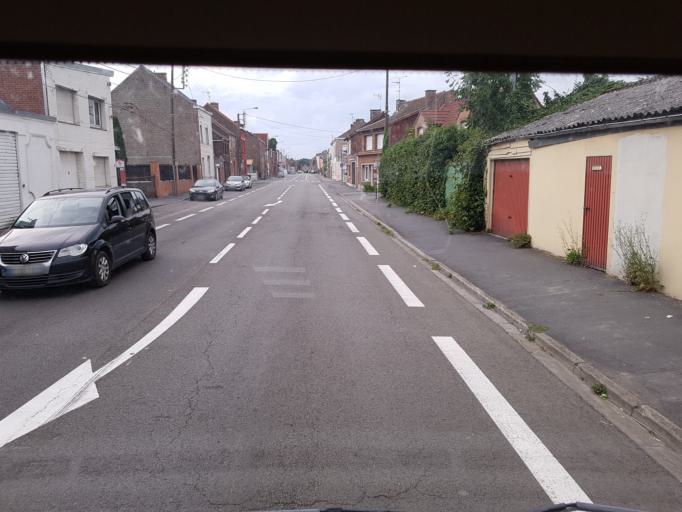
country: FR
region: Nord-Pas-de-Calais
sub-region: Departement du Nord
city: Conde-sur-l'Escaut
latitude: 50.4534
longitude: 3.5887
